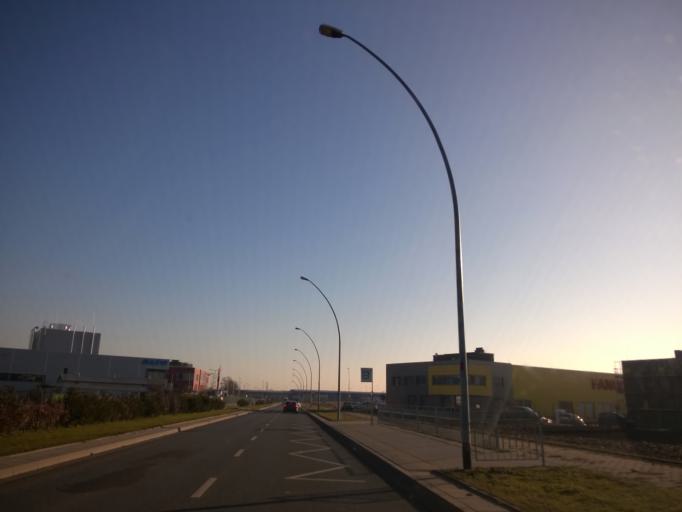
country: PL
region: Lower Silesian Voivodeship
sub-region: Powiat wroclawski
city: Bielany Wroclawskie
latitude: 51.0721
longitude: 16.9586
